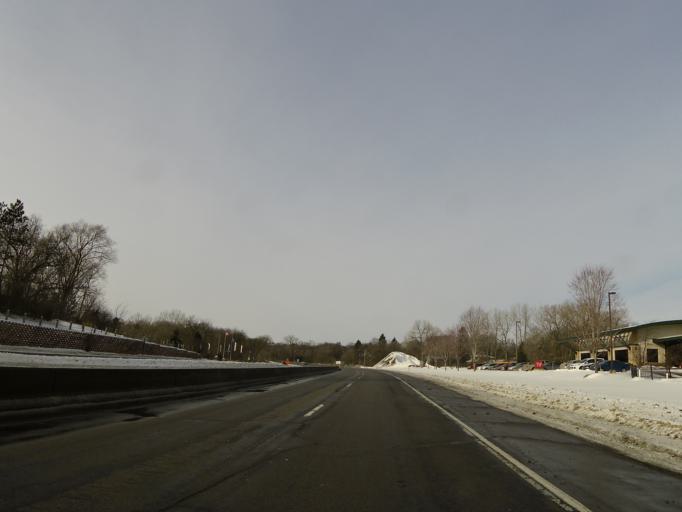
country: US
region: Minnesota
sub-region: Hennepin County
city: Minnetonka
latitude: 44.9113
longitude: -93.5165
